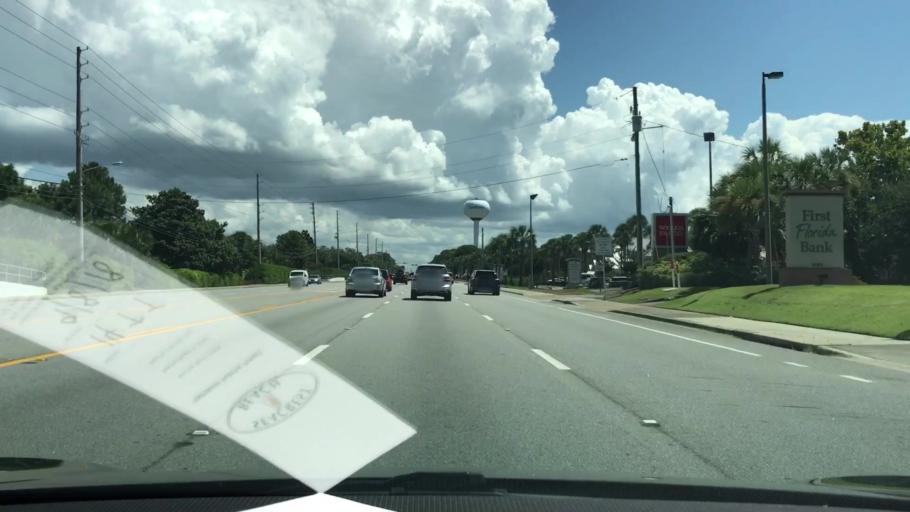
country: US
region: Florida
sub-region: Walton County
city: Miramar Beach
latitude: 30.3777
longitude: -86.3340
